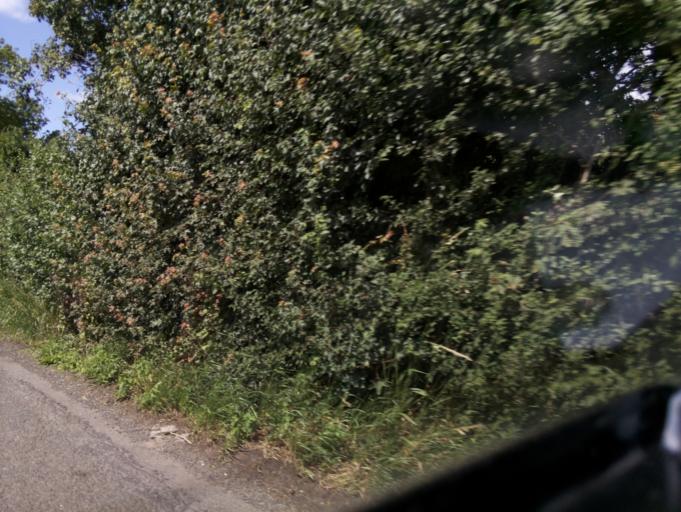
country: GB
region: England
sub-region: Nottinghamshire
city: Arnold
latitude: 53.0072
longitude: -1.0856
